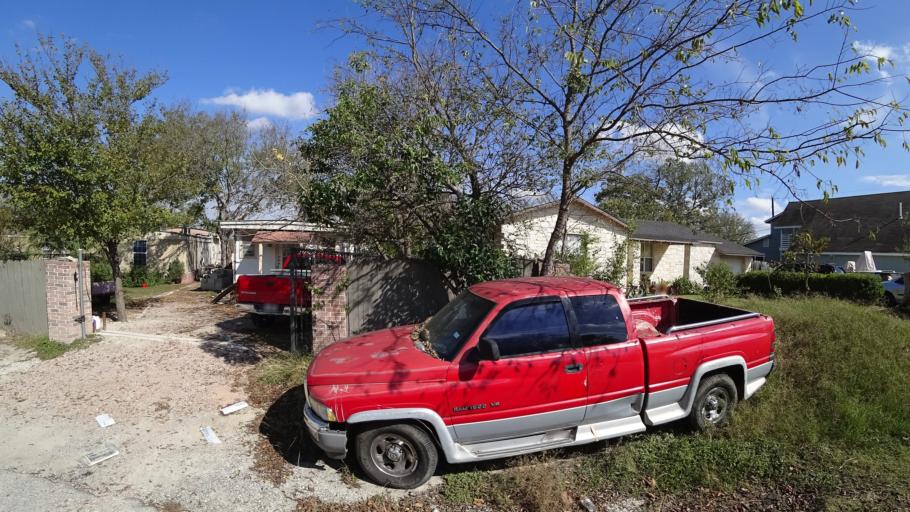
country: US
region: Texas
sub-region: Travis County
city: Windemere
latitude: 30.4517
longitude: -97.6397
